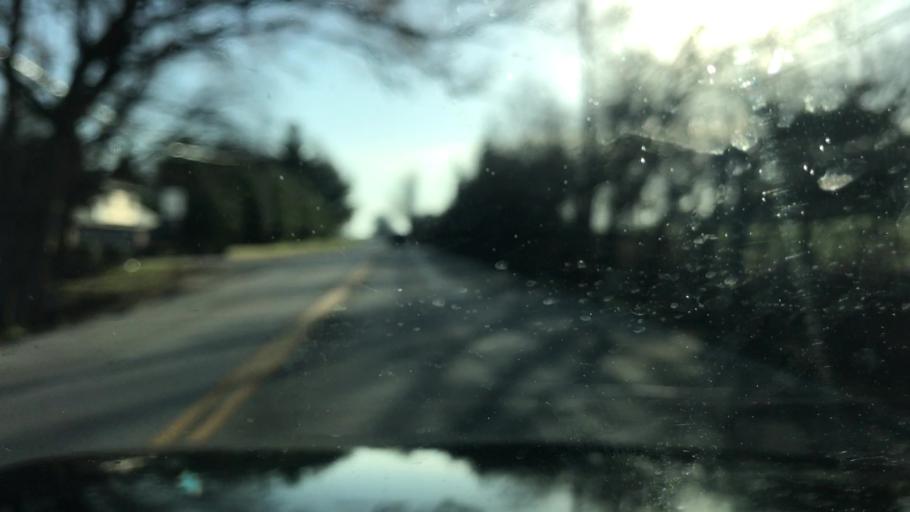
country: US
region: Indiana
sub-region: Vanderburgh County
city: Highland
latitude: 38.0376
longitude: -87.5538
